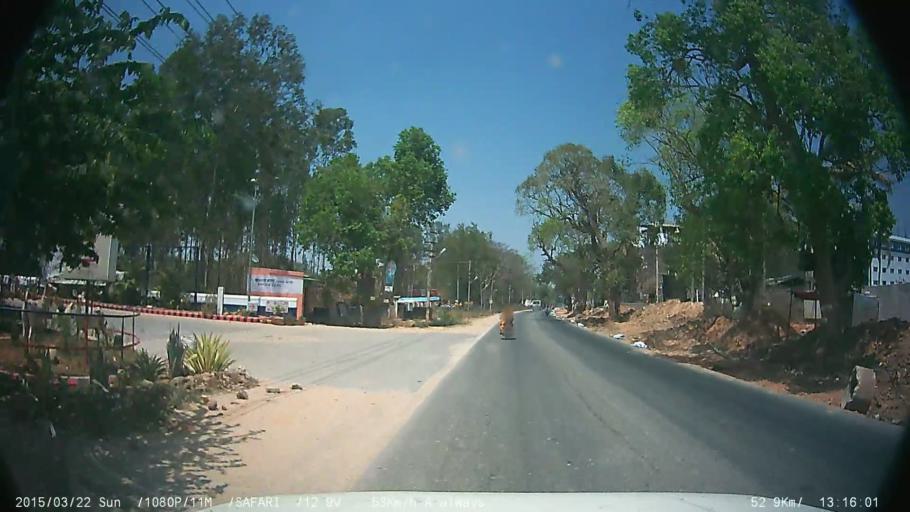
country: IN
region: Karnataka
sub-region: Bangalore Urban
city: Bangalore
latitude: 12.8273
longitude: 77.5867
